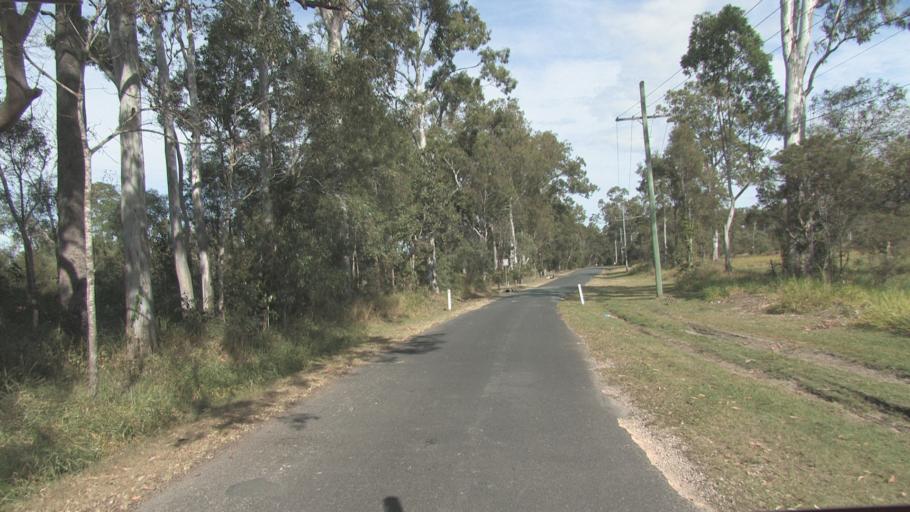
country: AU
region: Queensland
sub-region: Logan
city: Woodridge
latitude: -27.6643
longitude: 153.0859
